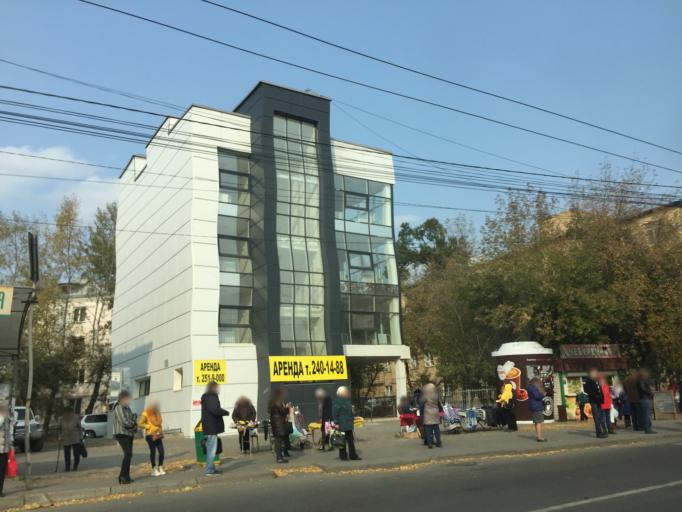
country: RU
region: Krasnoyarskiy
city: Krasnoyarsk
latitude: 56.0277
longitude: 92.9104
